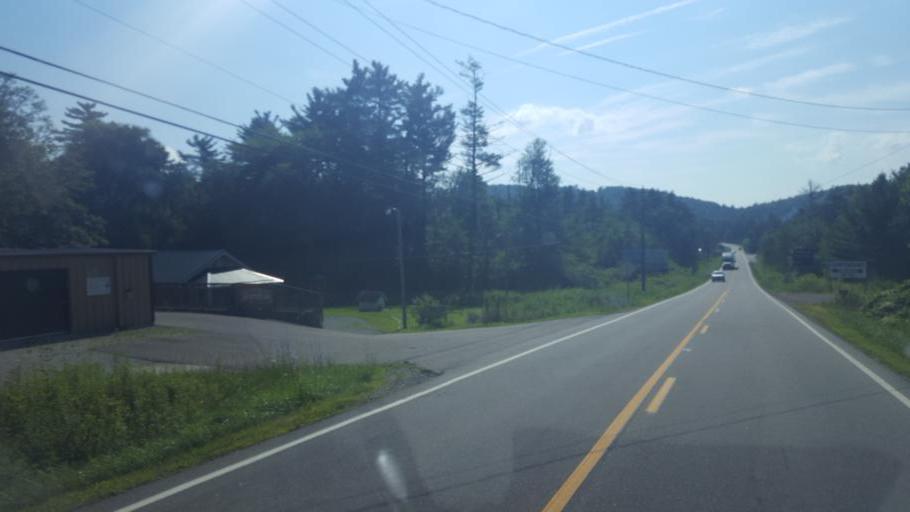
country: US
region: North Carolina
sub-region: Avery County
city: Newland
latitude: 36.0303
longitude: -81.9007
